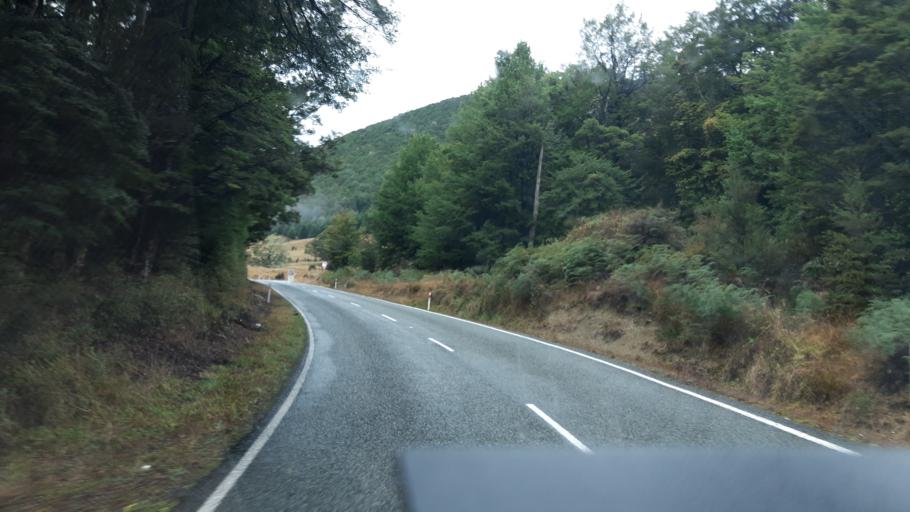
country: NZ
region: Tasman
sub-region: Tasman District
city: Wakefield
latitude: -41.7598
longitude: 172.8985
